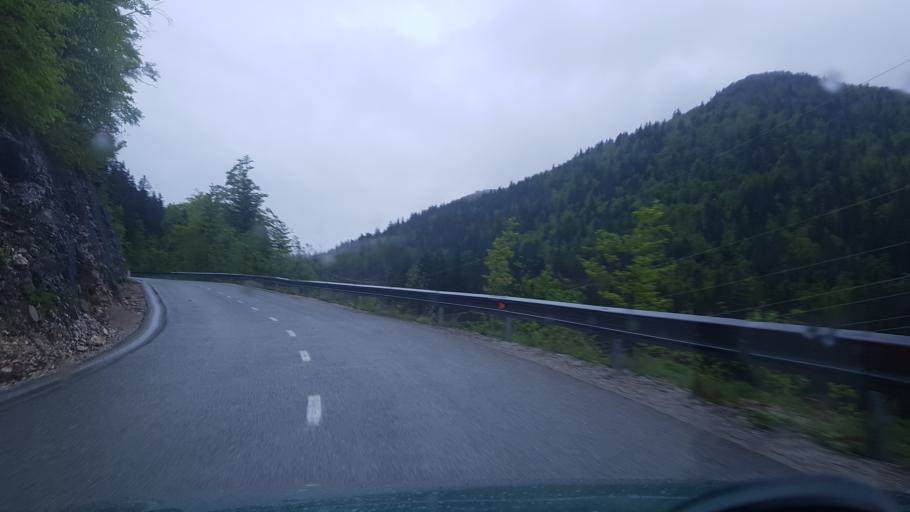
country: SI
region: Bohinj
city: Bohinjska Bistrica
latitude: 46.2518
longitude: 14.0042
